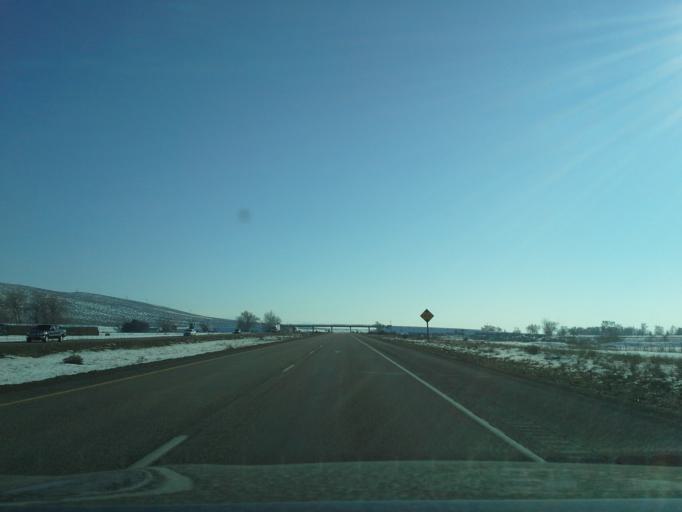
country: US
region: Idaho
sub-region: Bingham County
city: Blackfoot
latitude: 43.1288
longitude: -112.3889
